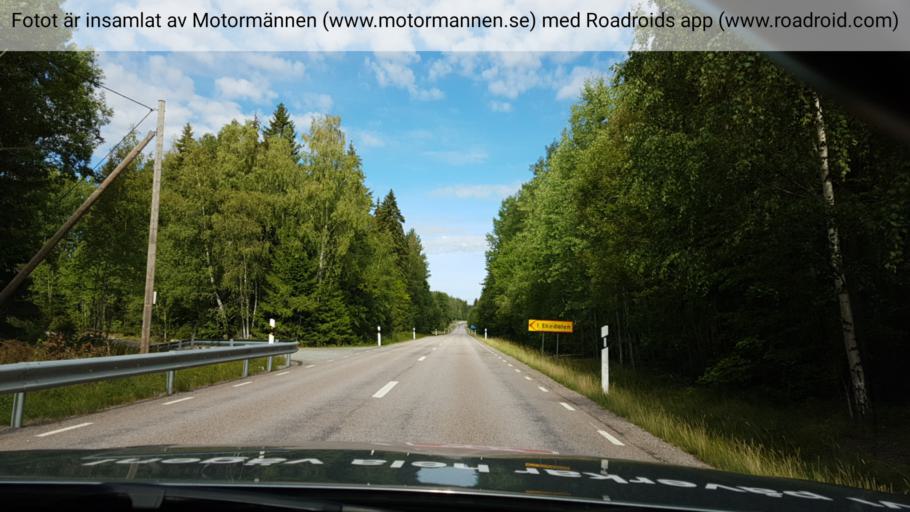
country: SE
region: Uppsala
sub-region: Heby Kommun
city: OEstervala
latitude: 59.9966
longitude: 17.3130
